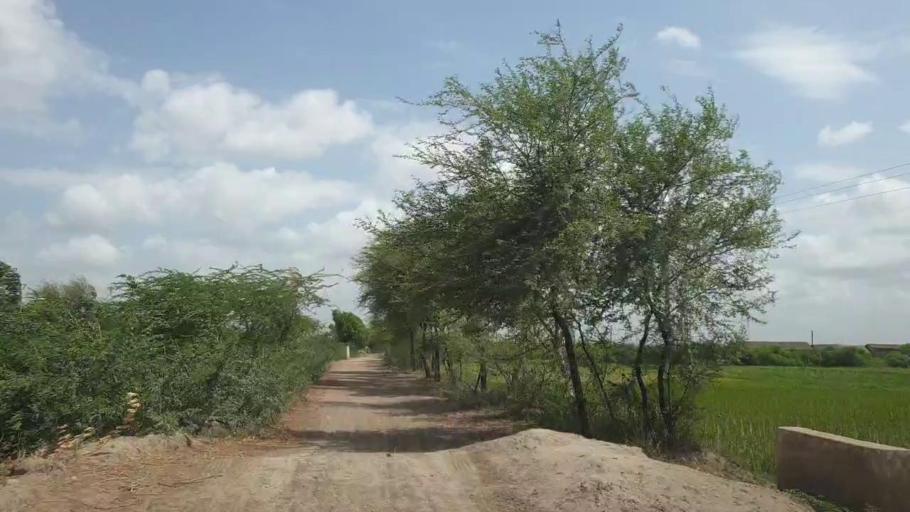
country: PK
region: Sindh
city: Tando Bago
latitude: 24.6510
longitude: 68.9931
